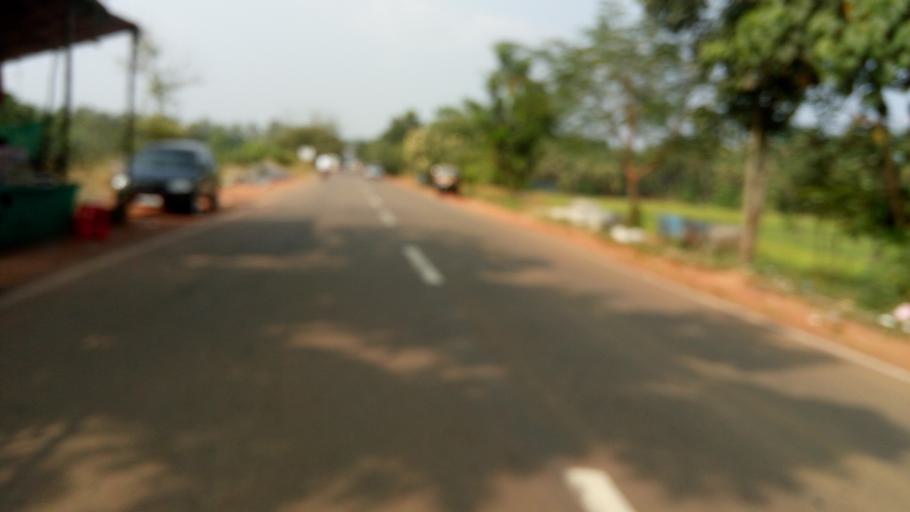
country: IN
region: Kerala
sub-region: Malappuram
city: Malappuram
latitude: 11.0010
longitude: 76.0147
